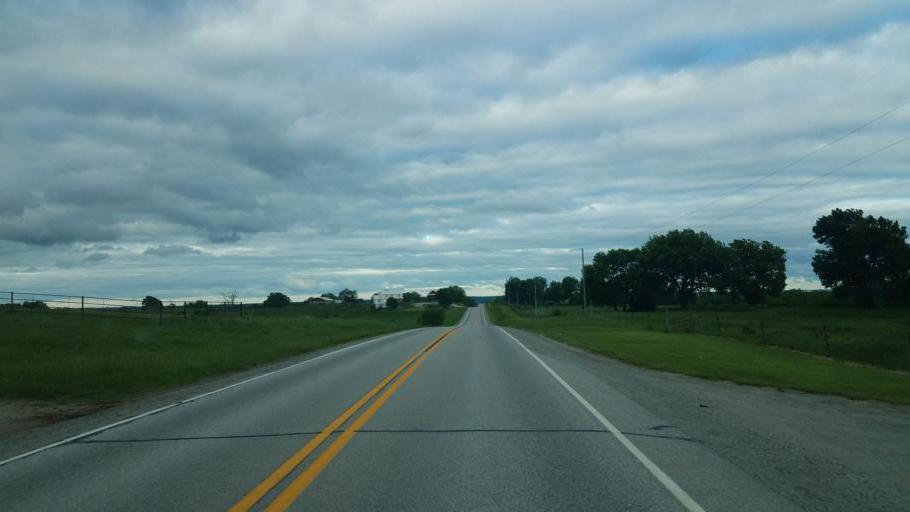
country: US
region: Iowa
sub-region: Decatur County
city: Lamoni
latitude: 40.6237
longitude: -93.8699
